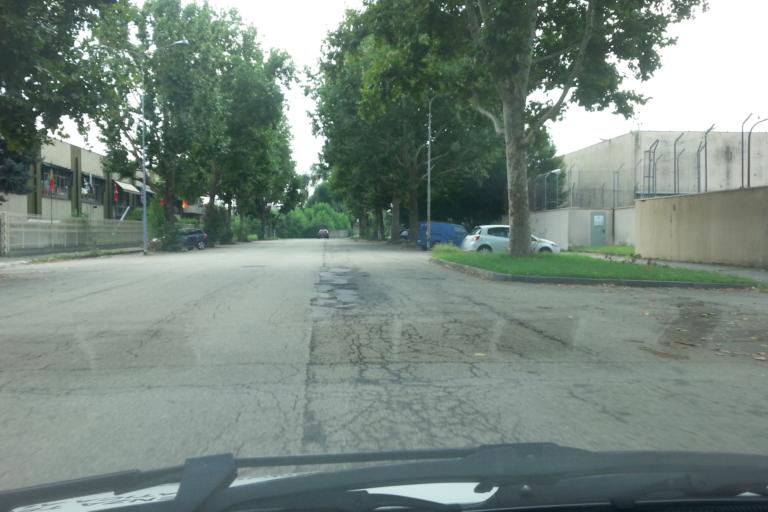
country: IT
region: Piedmont
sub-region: Provincia di Torino
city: Venaria Reale
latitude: 45.1134
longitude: 7.6481
